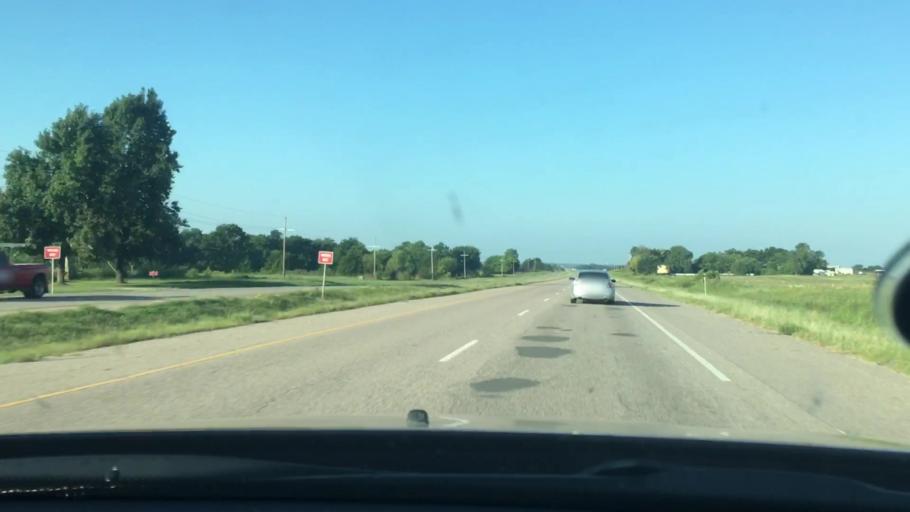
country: US
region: Oklahoma
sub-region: Pontotoc County
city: Ada
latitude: 34.6804
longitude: -96.7695
